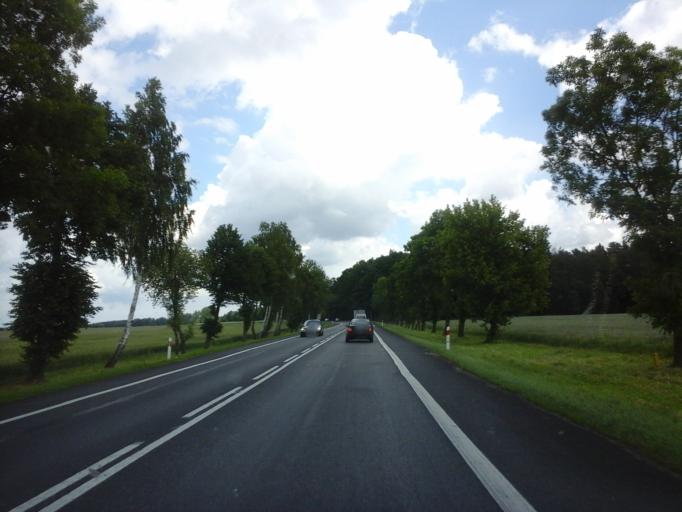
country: PL
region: West Pomeranian Voivodeship
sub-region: Powiat bialogardzki
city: Bialogard
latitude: 54.0868
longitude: 15.9866
